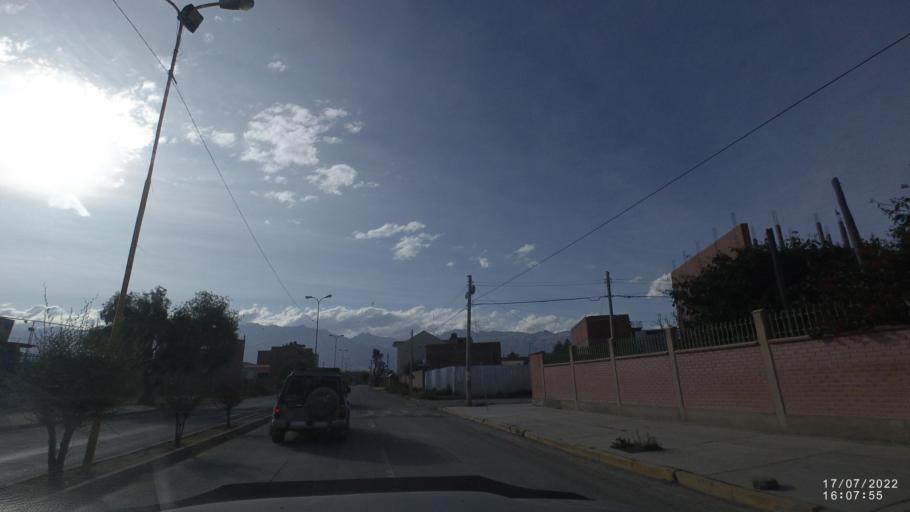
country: BO
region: Cochabamba
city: Sipe Sipe
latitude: -17.4115
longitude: -66.2724
